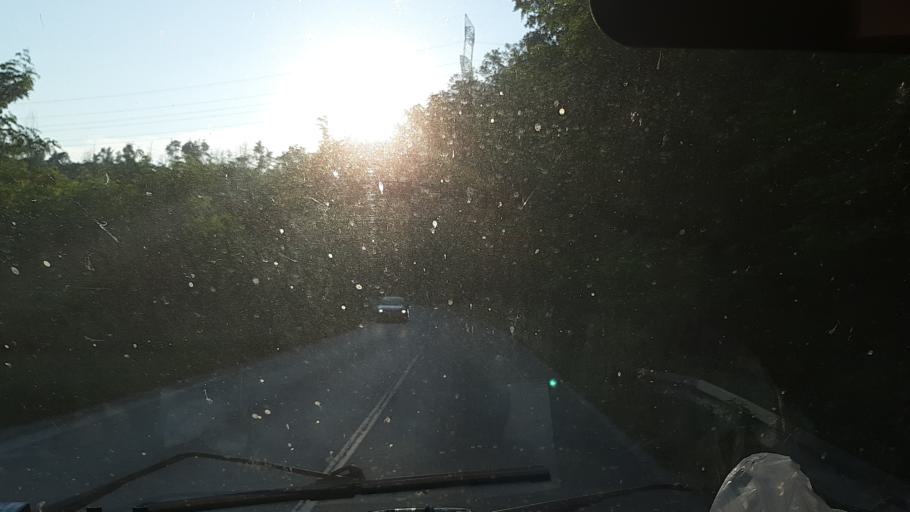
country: RO
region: Caras-Severin
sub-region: Municipiul Resita
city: Calnic
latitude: 45.3453
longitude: 21.8430
